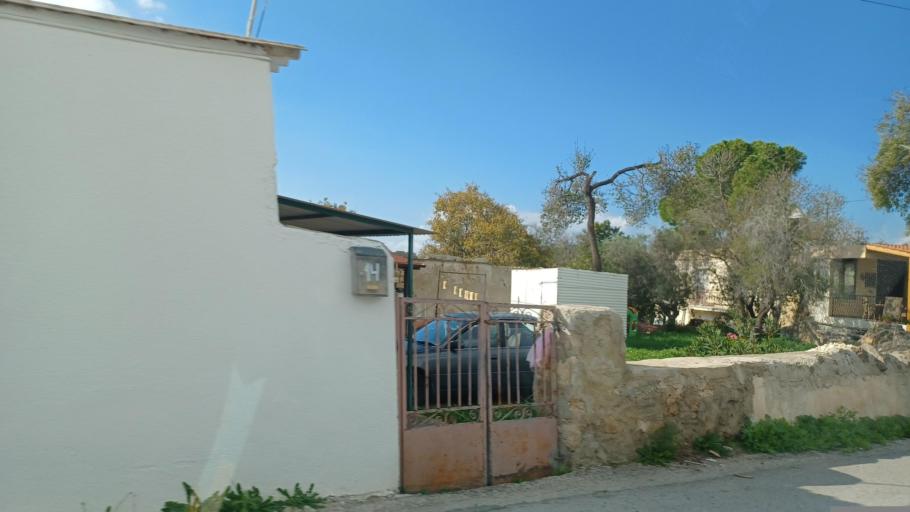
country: CY
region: Pafos
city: Mesogi
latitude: 34.7839
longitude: 32.4600
